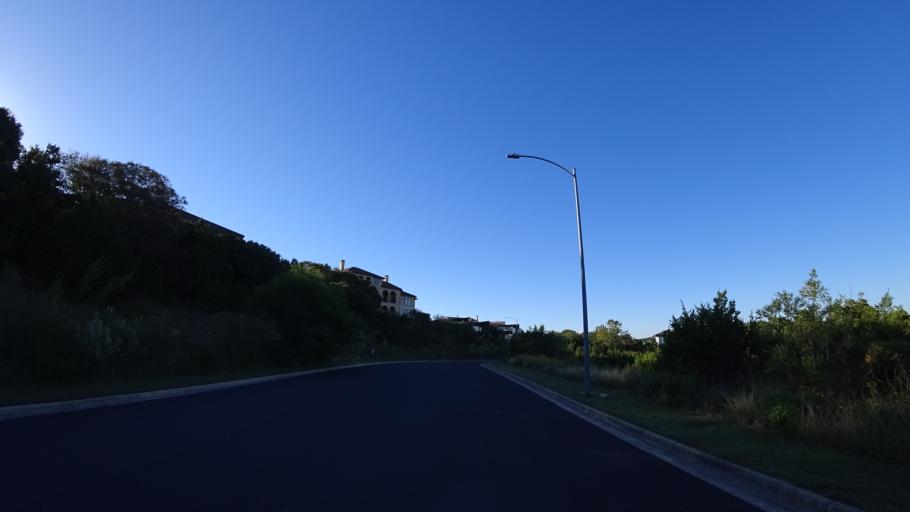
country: US
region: Texas
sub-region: Travis County
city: West Lake Hills
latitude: 30.3228
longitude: -97.8117
